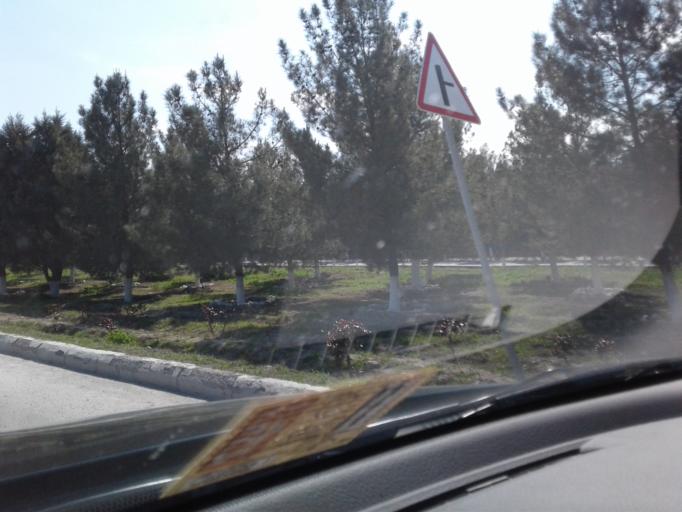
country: TM
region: Ahal
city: Abadan
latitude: 38.0633
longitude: 58.2585
